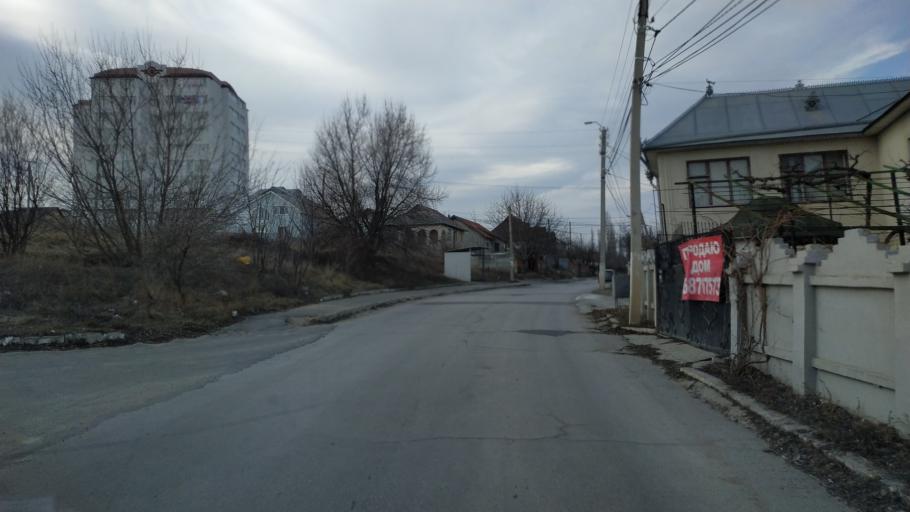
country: MD
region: Laloveni
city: Ialoveni
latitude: 46.9557
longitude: 28.7607
